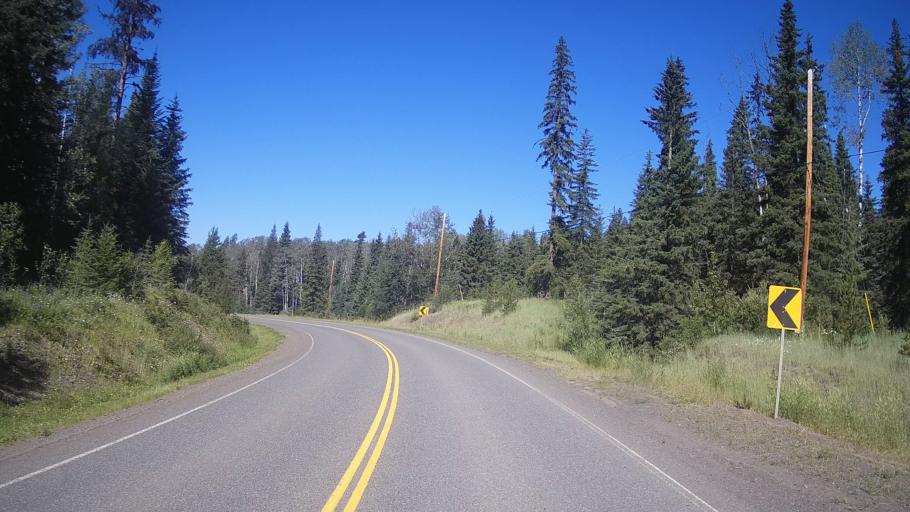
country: CA
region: British Columbia
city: Kamloops
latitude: 51.5055
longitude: -120.6037
